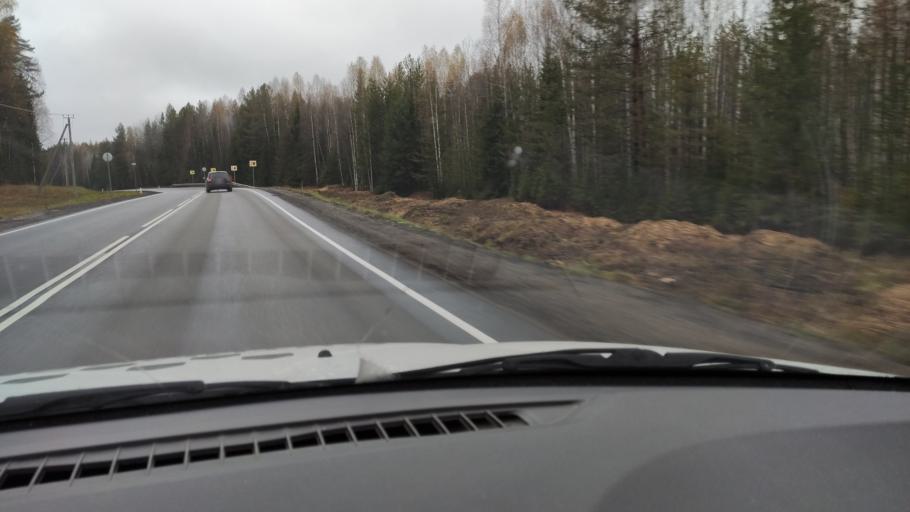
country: RU
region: Kirov
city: Dubrovka
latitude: 58.9131
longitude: 51.1666
